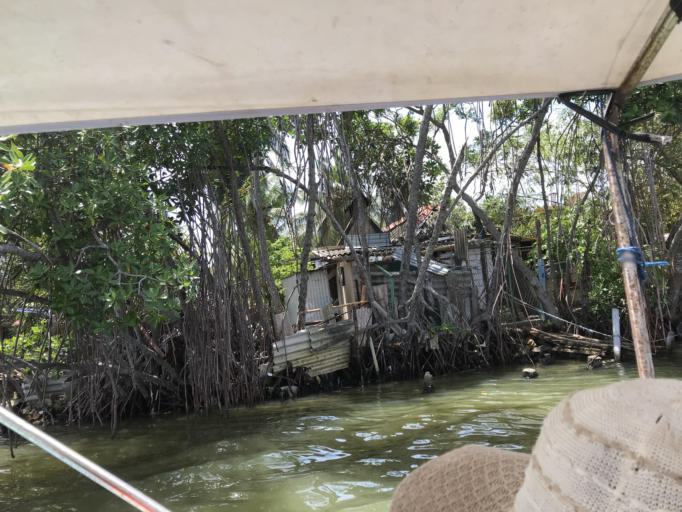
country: LK
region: Western
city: Negombo
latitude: 7.2019
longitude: 79.8305
